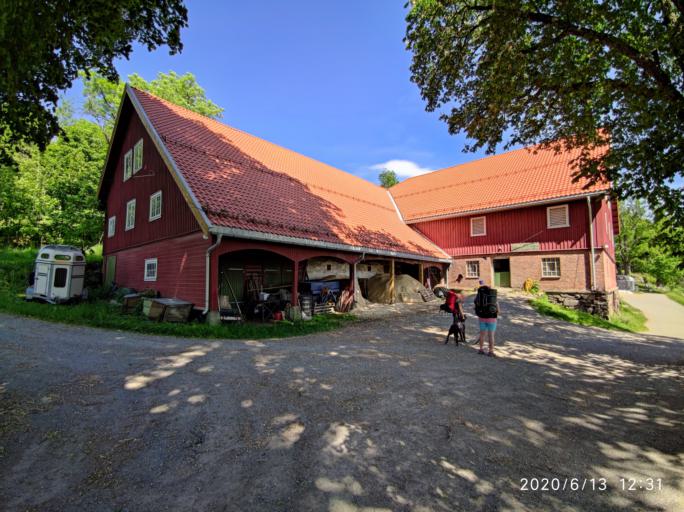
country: NO
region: Akershus
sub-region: Asker
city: Asker
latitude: 59.8597
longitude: 10.4110
